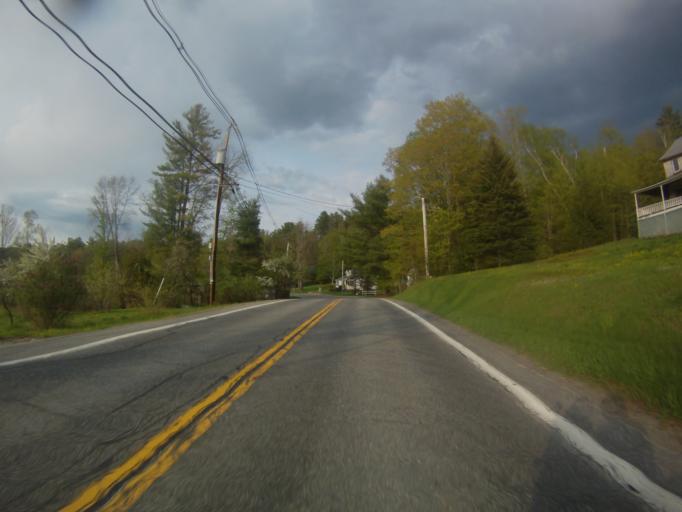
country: US
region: New York
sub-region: Warren County
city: Warrensburg
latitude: 43.6890
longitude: -73.7237
